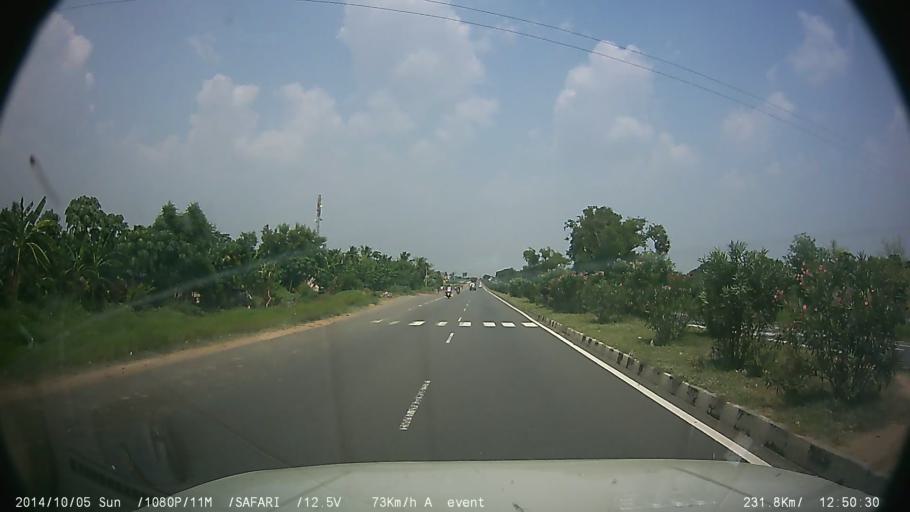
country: IN
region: Tamil Nadu
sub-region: Cuddalore
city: Vriddhachalam
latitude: 11.7157
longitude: 79.3343
